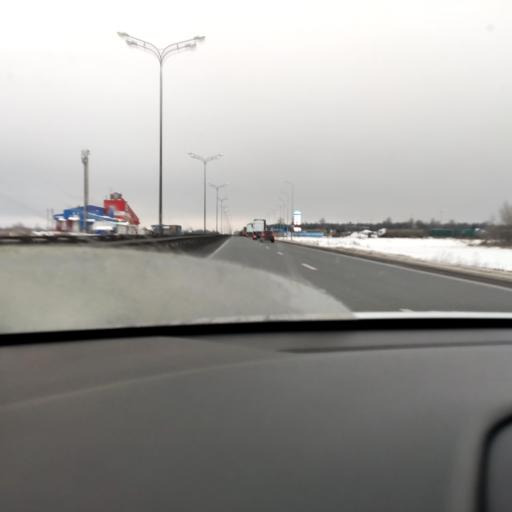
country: RU
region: Tatarstan
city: Osinovo
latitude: 55.7586
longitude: 48.8118
